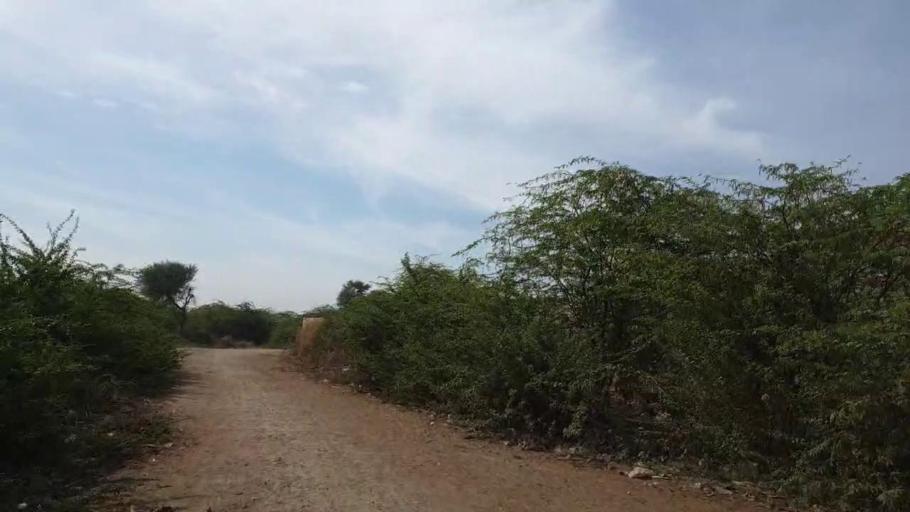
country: PK
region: Sindh
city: Kunri
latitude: 25.1632
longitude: 69.6175
